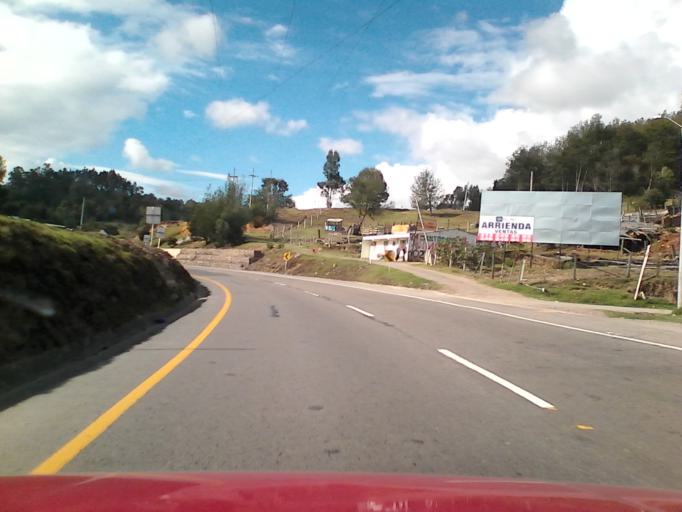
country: CO
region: Boyaca
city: Combita
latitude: 5.6498
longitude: -73.2861
